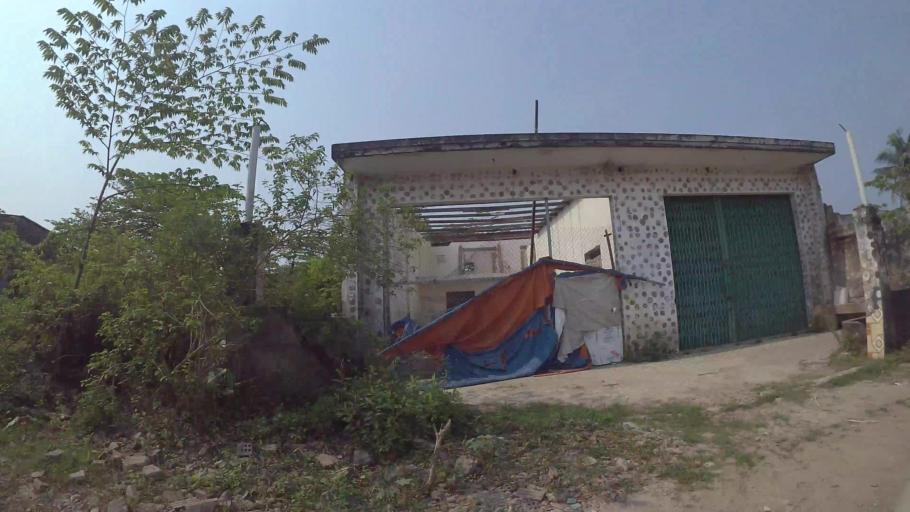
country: VN
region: Da Nang
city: Cam Le
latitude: 15.9975
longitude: 108.2169
